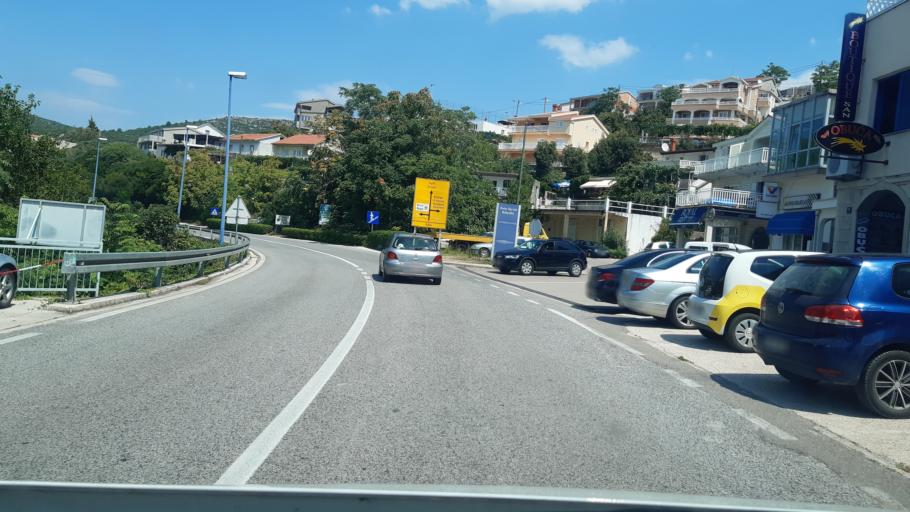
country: BA
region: Federation of Bosnia and Herzegovina
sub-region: Hercegovacko-Bosanski Kanton
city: Neum
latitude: 42.9243
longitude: 17.6167
